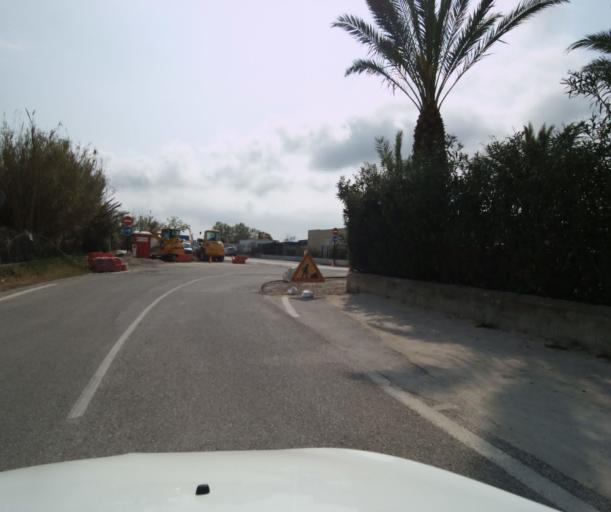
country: FR
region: Provence-Alpes-Cote d'Azur
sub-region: Departement du Var
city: Hyeres
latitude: 43.1029
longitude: 6.1434
